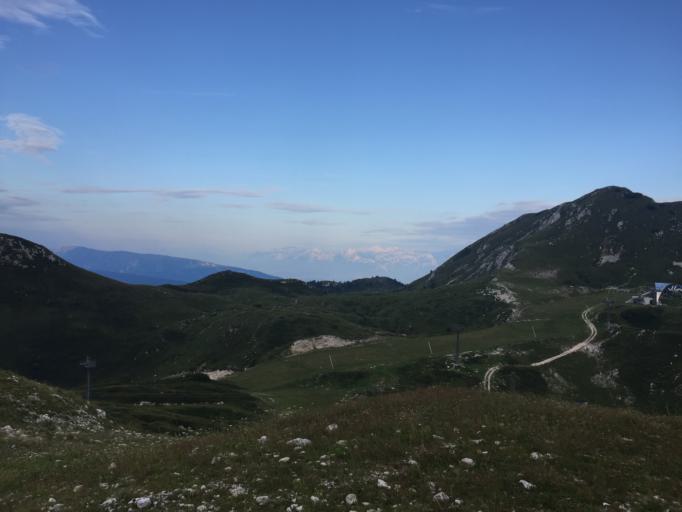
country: IT
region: Friuli Venezia Giulia
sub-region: Provincia di Pordenone
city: Polcenigo
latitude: 46.1125
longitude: 12.4959
